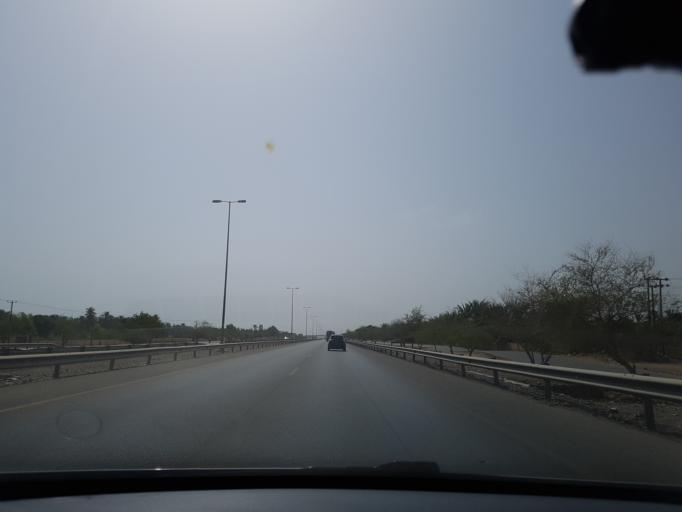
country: OM
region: Al Batinah
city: Al Khaburah
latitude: 23.9357
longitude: 57.1350
